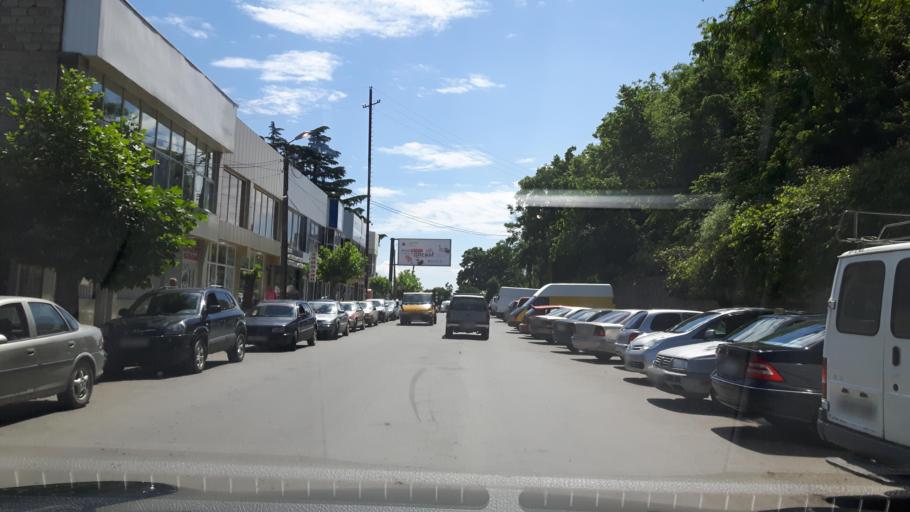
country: GE
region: Kakheti
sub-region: Telavi
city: Telavi
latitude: 41.9217
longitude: 45.4720
